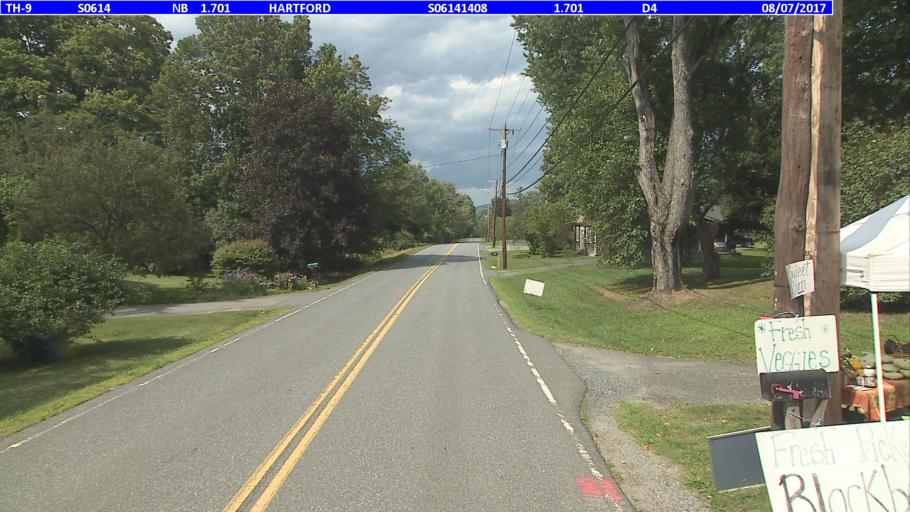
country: US
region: Vermont
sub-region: Windsor County
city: Wilder
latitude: 43.6784
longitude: -72.3230
